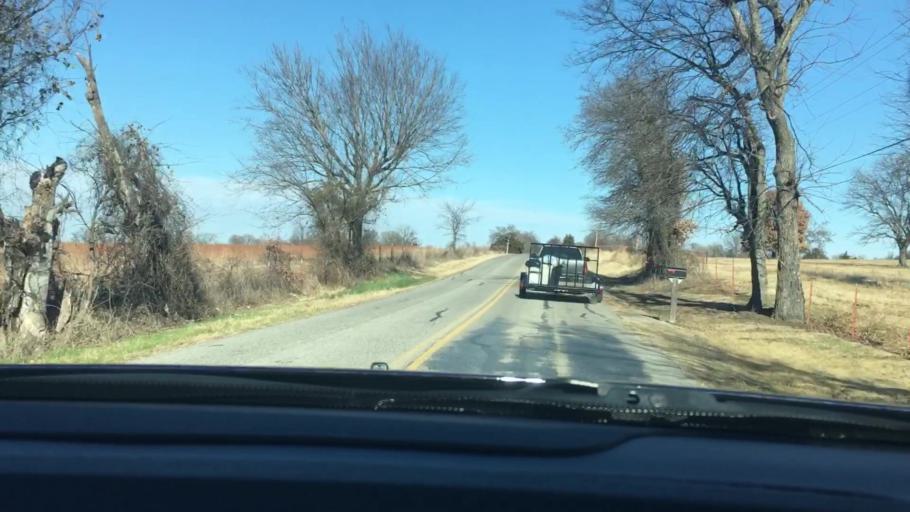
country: US
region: Oklahoma
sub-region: Murray County
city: Davis
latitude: 34.4853
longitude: -97.0556
